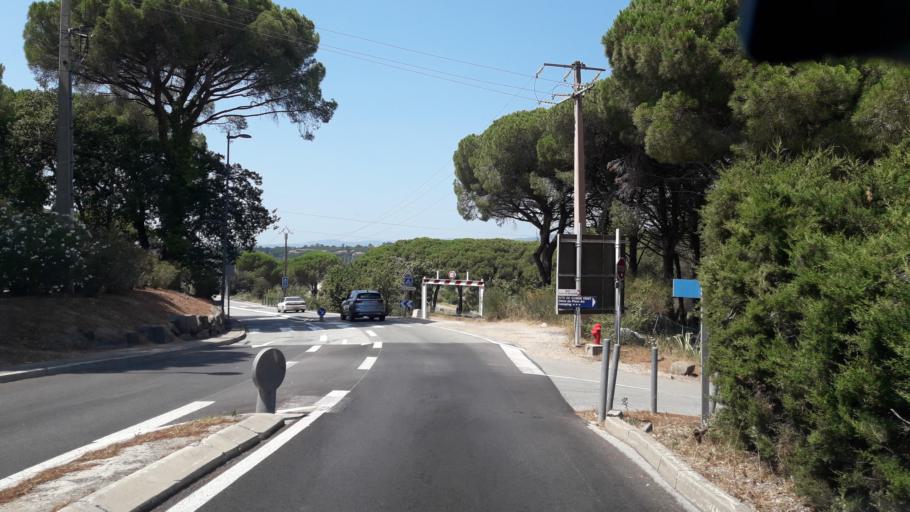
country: FR
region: Provence-Alpes-Cote d'Azur
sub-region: Departement du Var
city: Frejus
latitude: 43.4503
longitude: 6.7471
